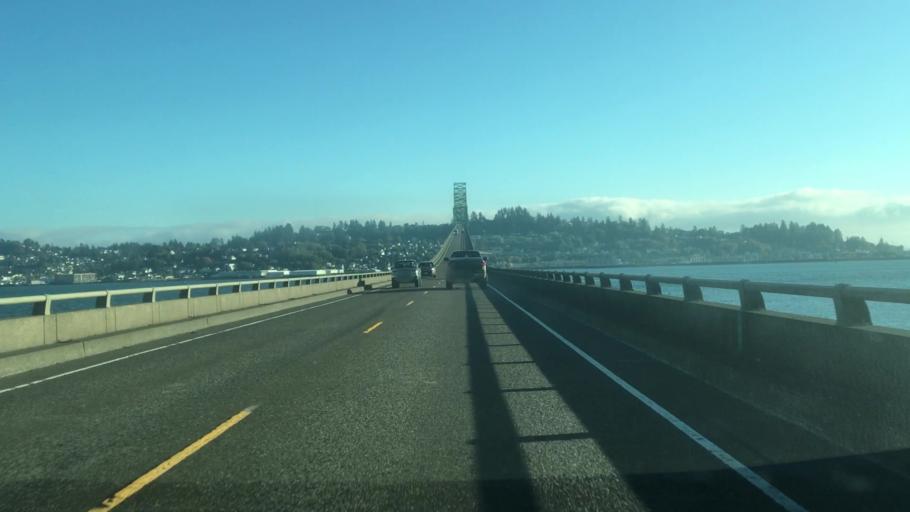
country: US
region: Oregon
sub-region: Clatsop County
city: Astoria
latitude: 46.2042
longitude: -123.8564
